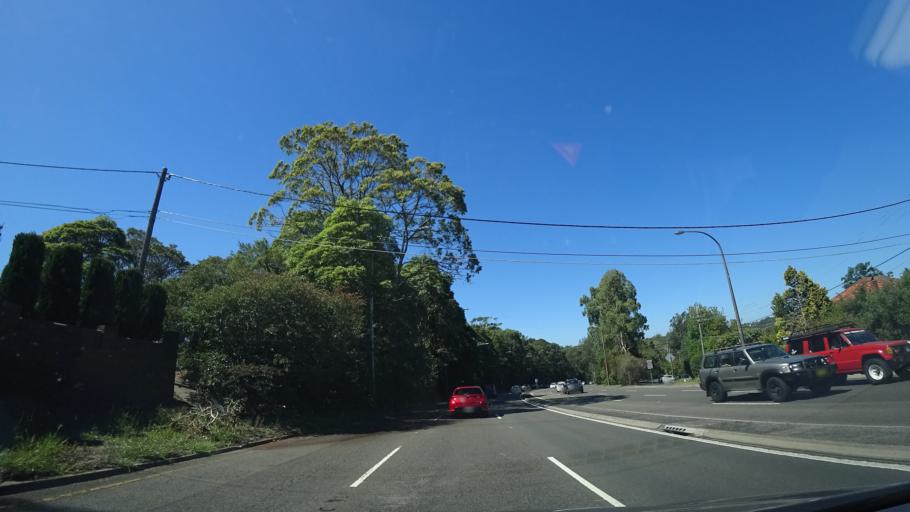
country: AU
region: New South Wales
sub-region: Ku-ring-gai
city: Roseville Chase
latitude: -33.7769
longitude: 151.1952
